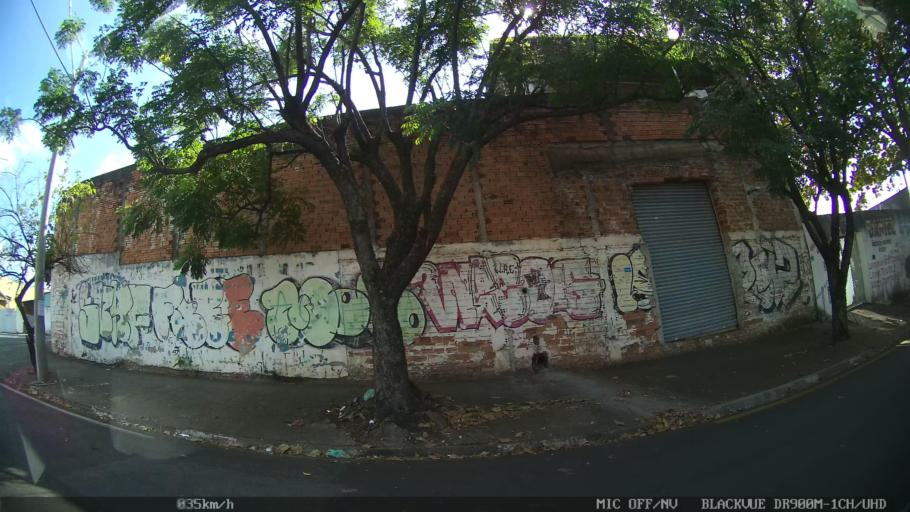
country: BR
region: Sao Paulo
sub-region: Campinas
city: Campinas
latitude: -22.9404
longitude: -47.1159
